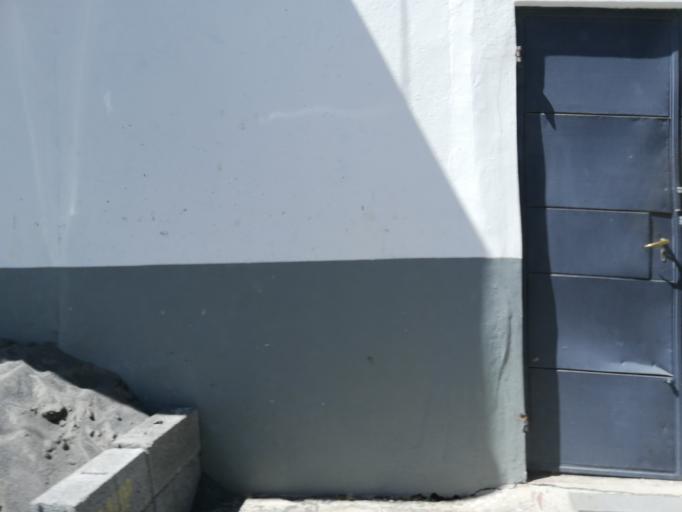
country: MU
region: Port Louis
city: Port Louis
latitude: -20.1711
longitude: 57.4982
